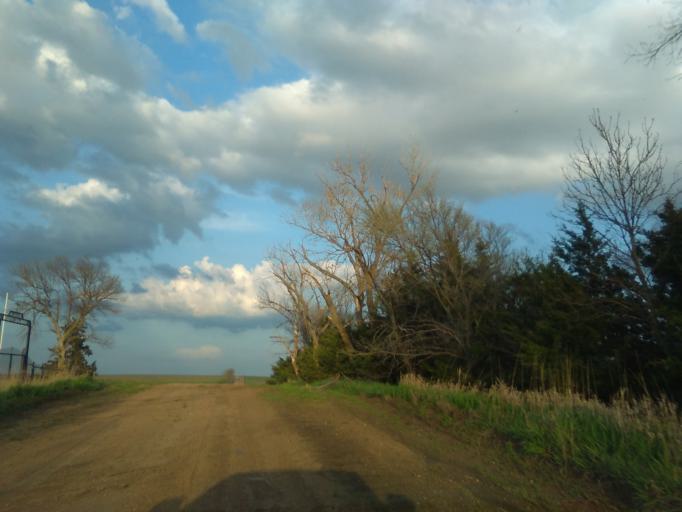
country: US
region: Nebraska
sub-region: Webster County
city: Red Cloud
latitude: 40.2054
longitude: -98.3736
